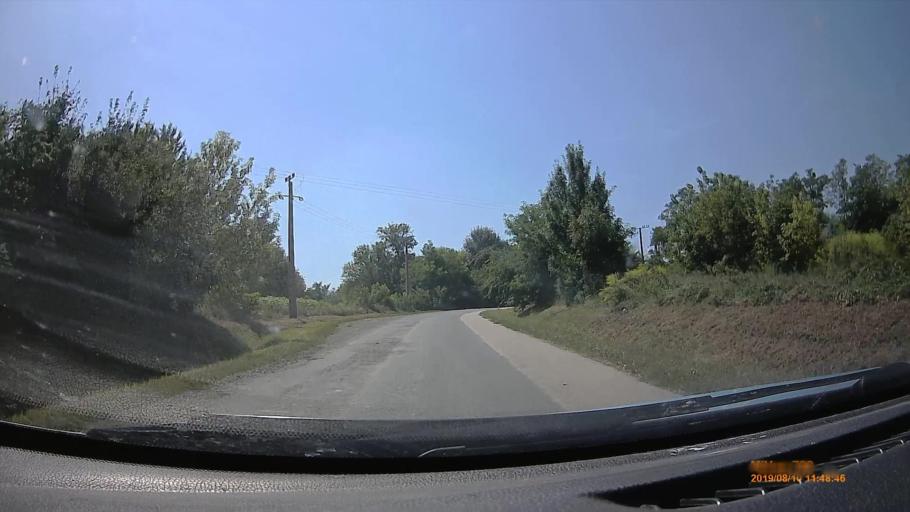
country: HU
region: Somogy
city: Somogyvar
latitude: 46.5018
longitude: 17.7347
